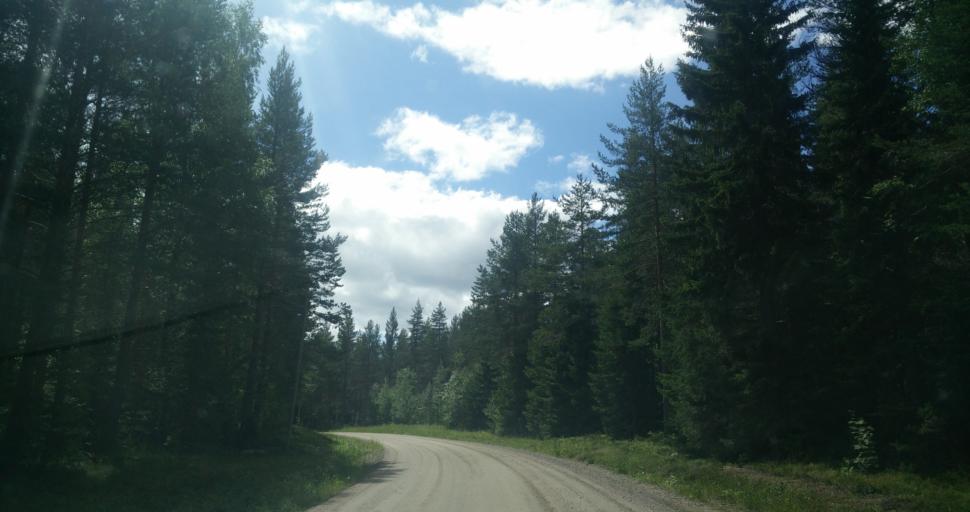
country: SE
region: Vaesternorrland
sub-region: Sundsvalls Kommun
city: Vi
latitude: 62.1466
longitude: 17.1362
